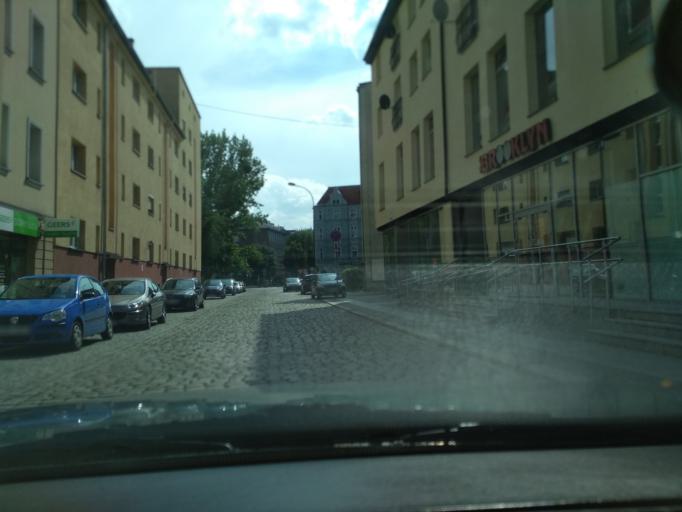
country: PL
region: Silesian Voivodeship
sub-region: Powiat raciborski
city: Raciborz
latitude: 50.0907
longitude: 18.2176
